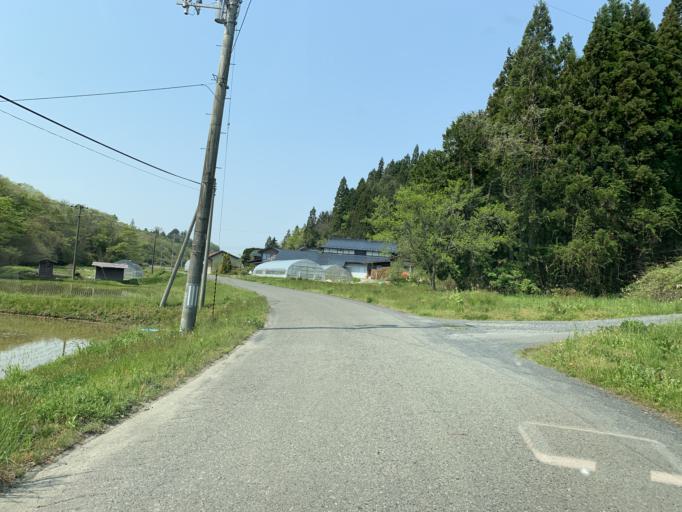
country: JP
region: Iwate
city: Ichinoseki
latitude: 38.8939
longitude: 141.0766
